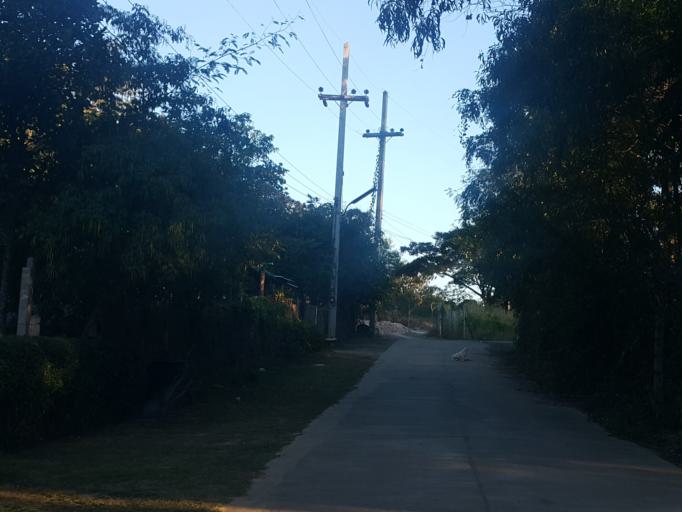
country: TH
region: Chiang Mai
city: San Sai
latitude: 18.8692
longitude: 99.1410
